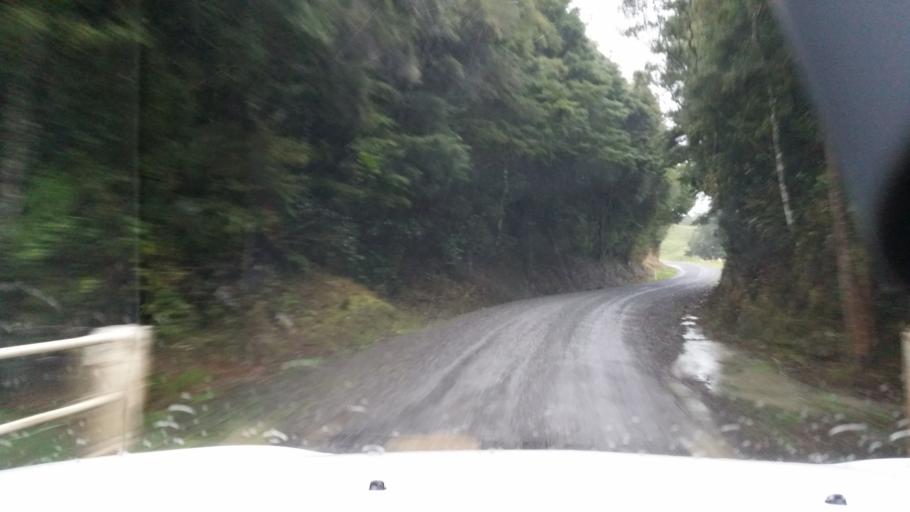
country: NZ
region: Northland
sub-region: Kaipara District
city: Dargaville
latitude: -35.7430
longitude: 173.9621
